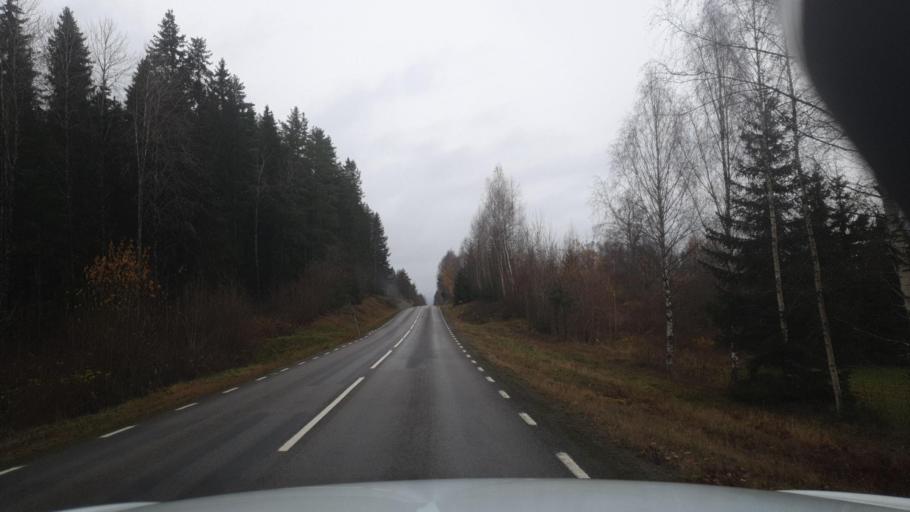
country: SE
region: Vaermland
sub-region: Arvika Kommun
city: Arvika
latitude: 59.6196
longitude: 12.5085
